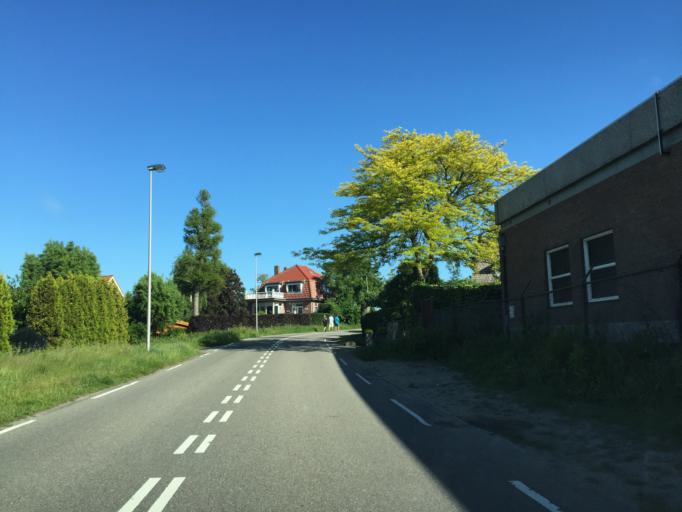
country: NL
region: South Holland
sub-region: Gemeente Lansingerland
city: Bergschenhoek
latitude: 51.9942
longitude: 4.5190
